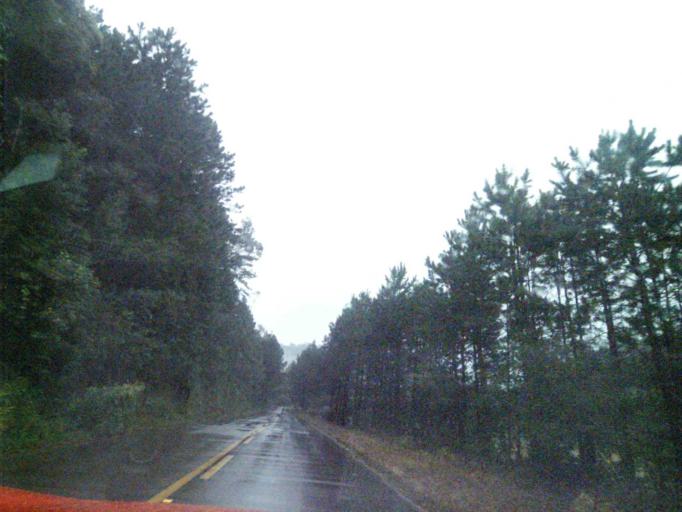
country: BR
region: Santa Catarina
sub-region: Anitapolis
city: Anitapolis
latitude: -27.8396
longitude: -49.0519
